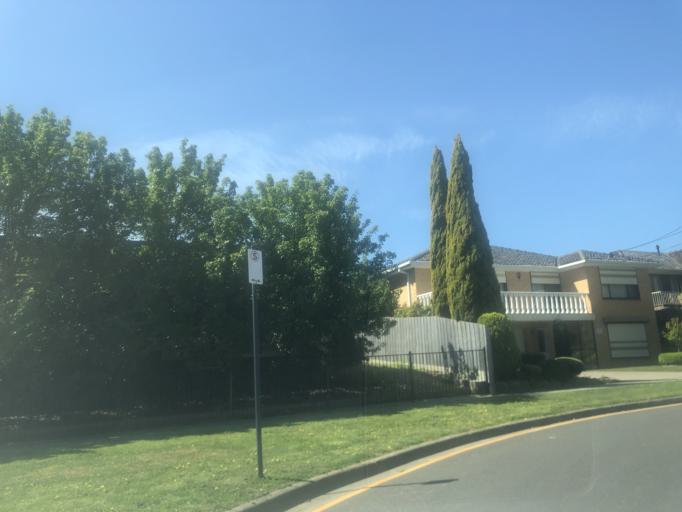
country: AU
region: Victoria
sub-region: Monash
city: Mulgrave
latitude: -37.9019
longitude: 145.1785
